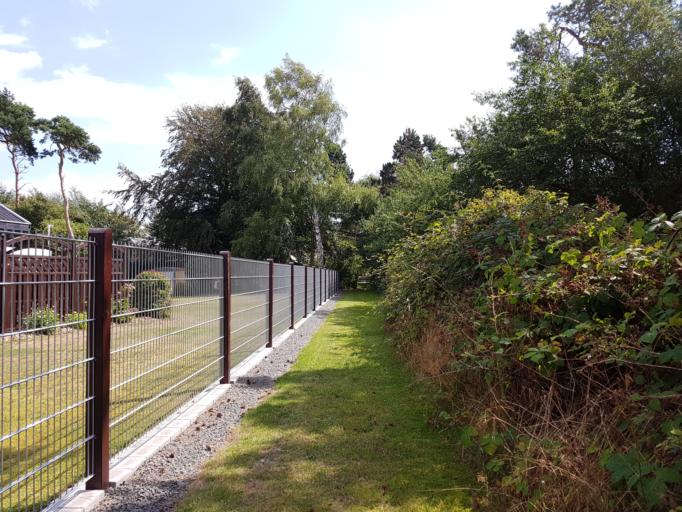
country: DK
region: Zealand
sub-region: Guldborgsund Kommune
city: Nykobing Falster
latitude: 54.5717
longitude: 11.9369
